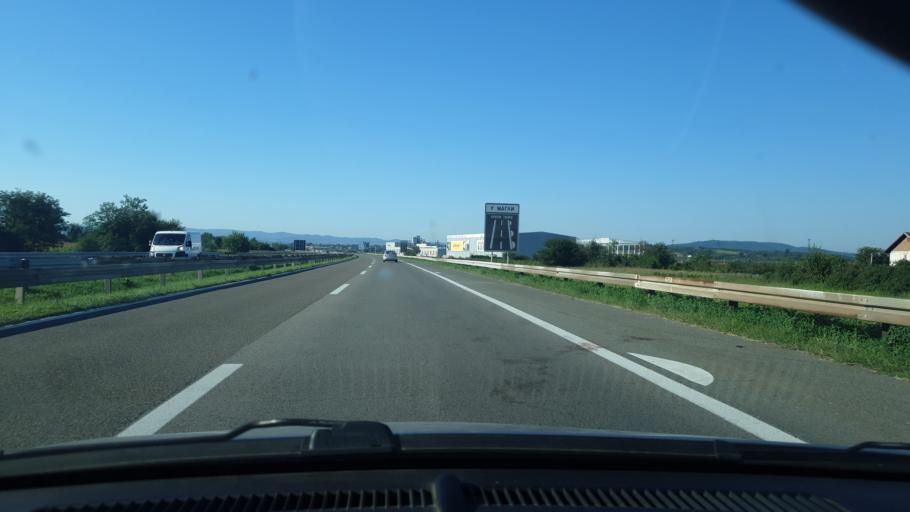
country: RS
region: Central Serbia
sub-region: Sumadijski Okrug
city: Lapovo
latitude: 44.1795
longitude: 21.1107
